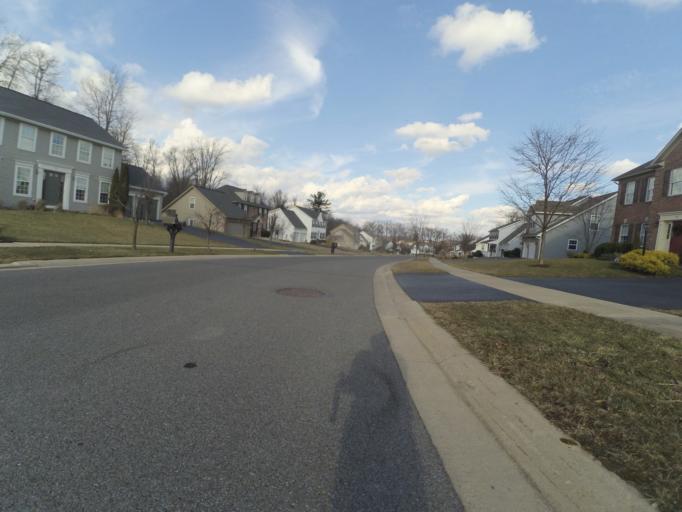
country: US
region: Pennsylvania
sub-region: Centre County
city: Park Forest Village
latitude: 40.8032
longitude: -77.9598
